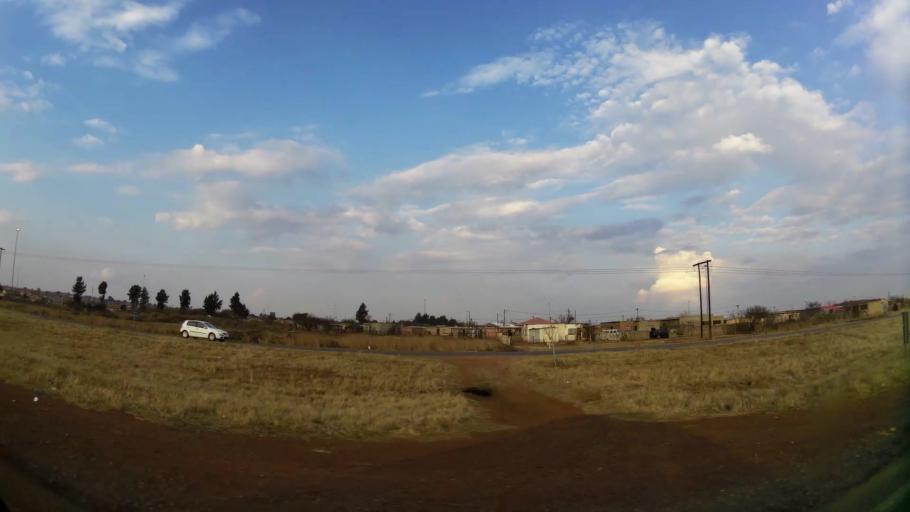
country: ZA
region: Gauteng
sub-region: City of Johannesburg Metropolitan Municipality
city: Orange Farm
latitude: -26.5923
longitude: 27.8209
